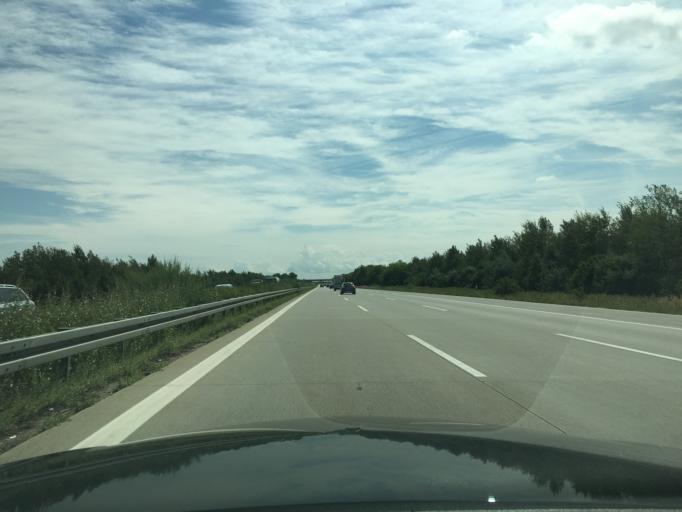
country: DE
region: Saxony
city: Wiedemar
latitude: 51.4909
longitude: 12.2058
